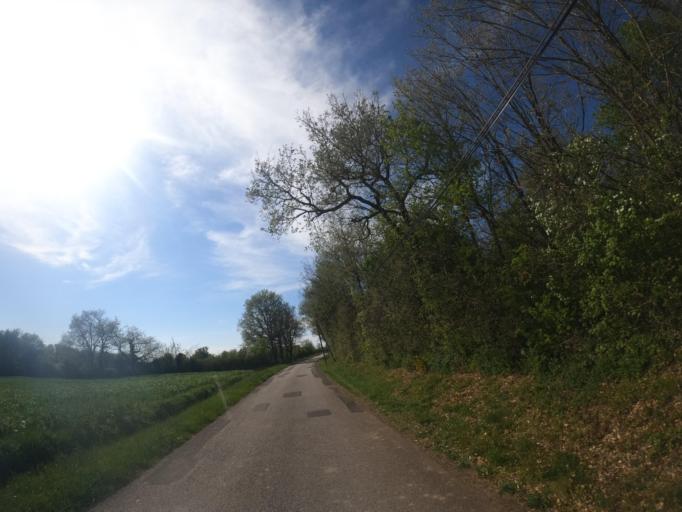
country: FR
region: Poitou-Charentes
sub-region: Departement des Deux-Sevres
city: Saint-Jean-de-Thouars
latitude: 46.9266
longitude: -0.2155
